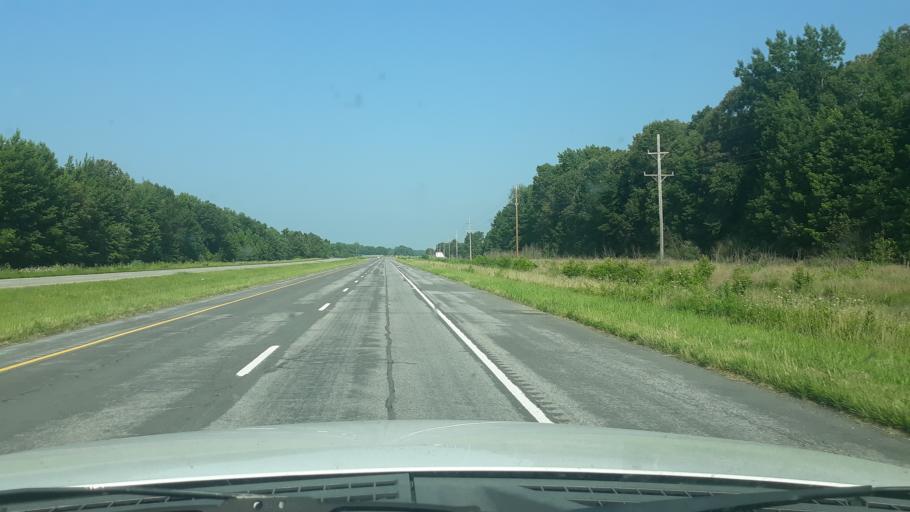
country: US
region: Illinois
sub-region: Saline County
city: Carrier Mills
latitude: 37.7336
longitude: -88.6633
